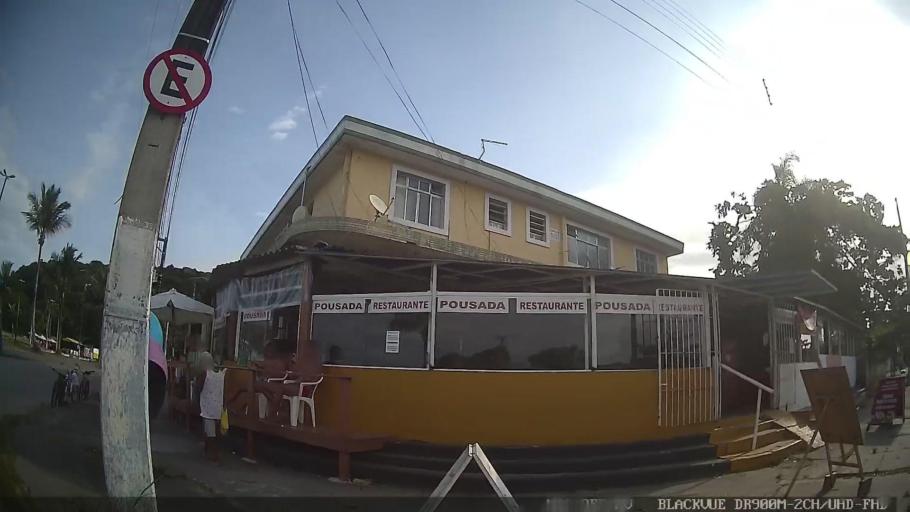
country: BR
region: Sao Paulo
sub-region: Bertioga
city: Bertioga
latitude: -23.8165
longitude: -46.0419
